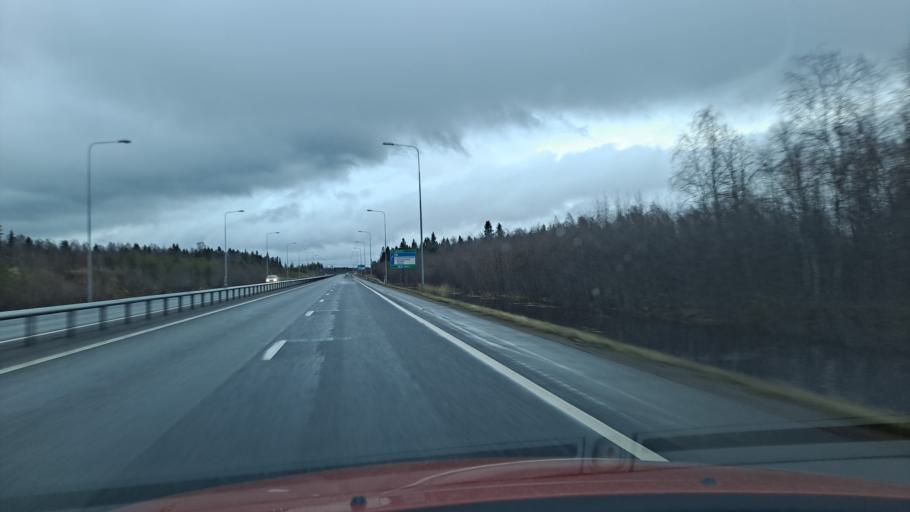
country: FI
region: Lapland
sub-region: Kemi-Tornio
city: Kemi
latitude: 65.7063
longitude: 24.6443
